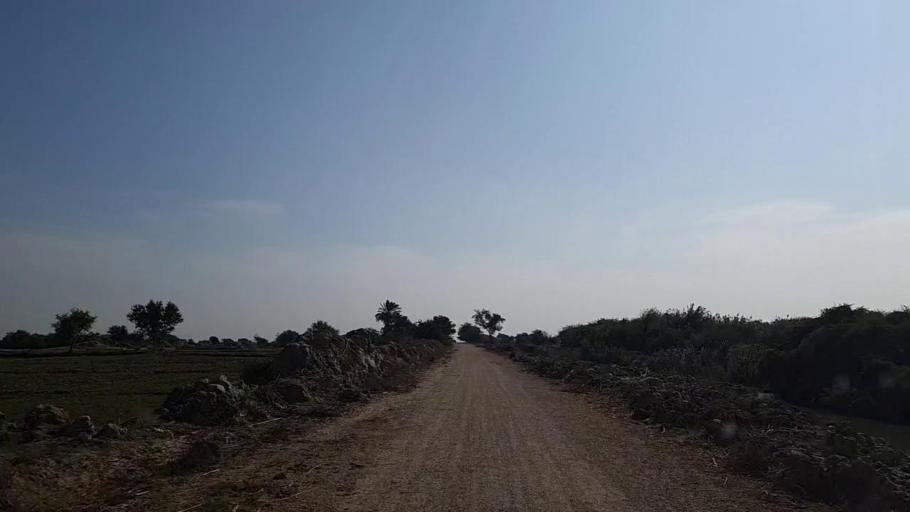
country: PK
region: Sindh
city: Daro Mehar
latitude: 24.7206
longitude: 68.1157
